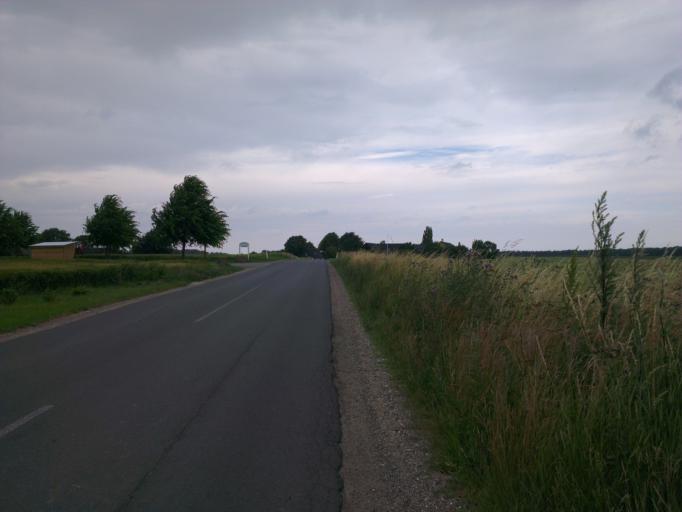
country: DK
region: Capital Region
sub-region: Frederikssund Kommune
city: Skibby
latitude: 55.7667
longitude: 11.9486
